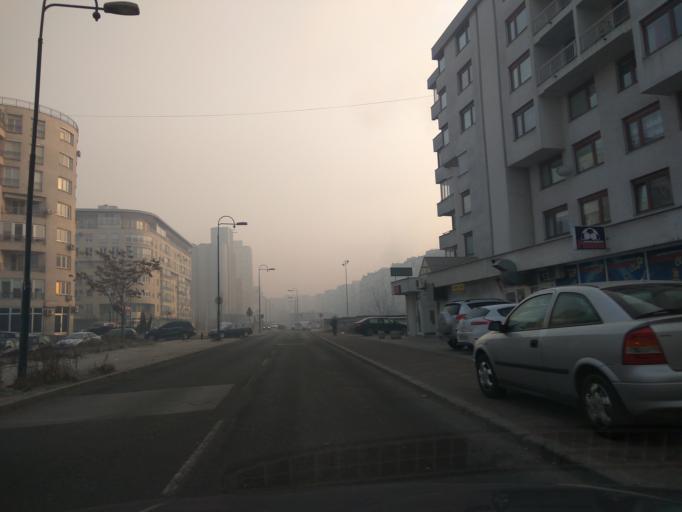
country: BA
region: Federation of Bosnia and Herzegovina
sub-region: Kanton Sarajevo
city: Sarajevo
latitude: 43.8523
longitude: 18.3707
